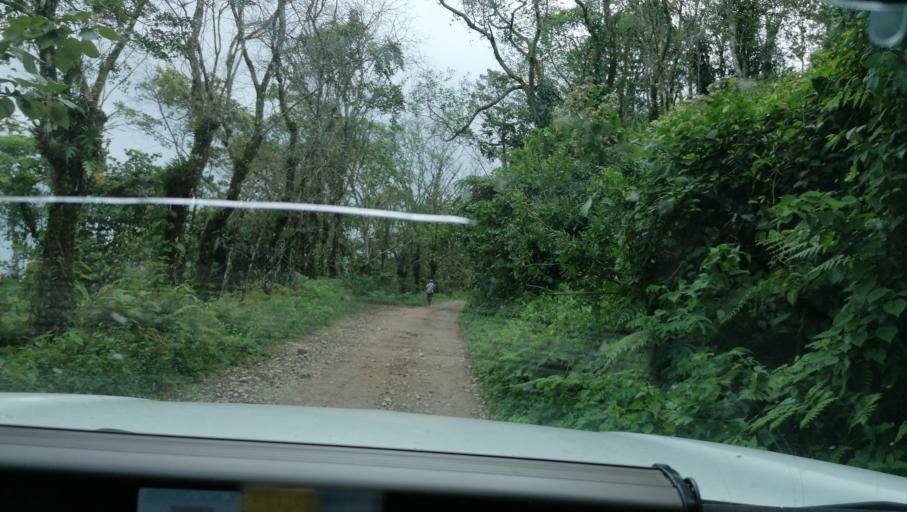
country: MX
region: Chiapas
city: Ixtacomitan
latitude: 17.3520
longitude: -93.1452
